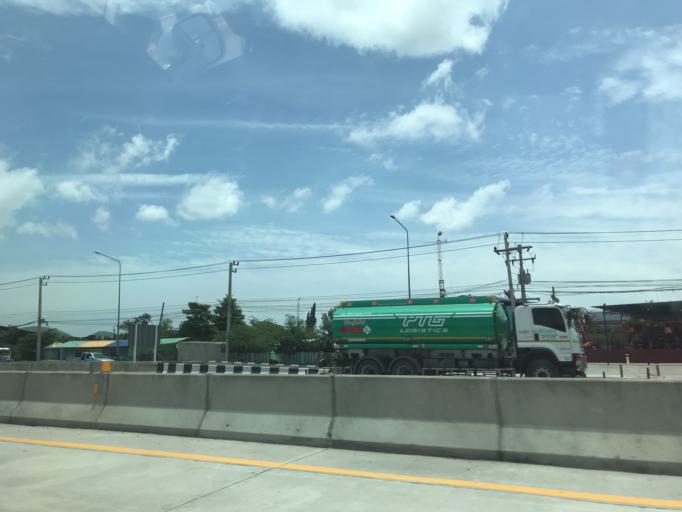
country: TH
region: Chon Buri
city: Ban Talat Bueng
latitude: 13.1143
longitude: 100.9669
